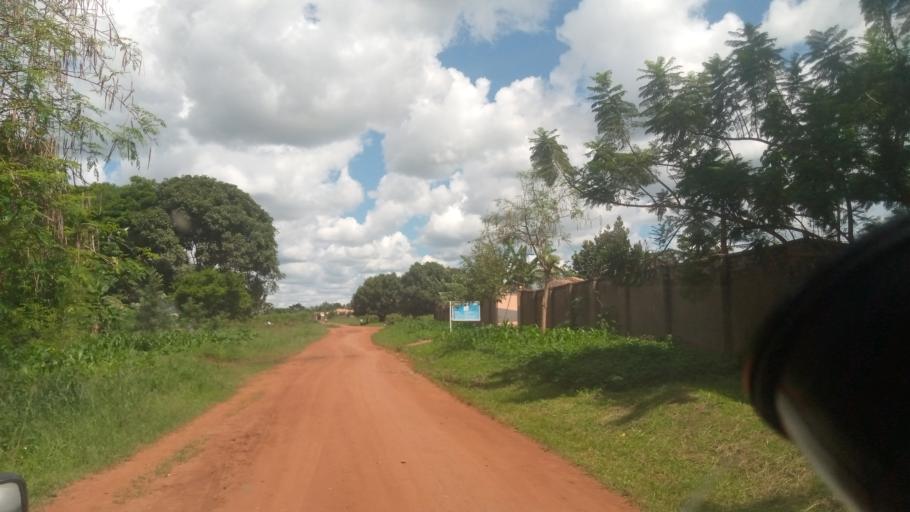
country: UG
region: Northern Region
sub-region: Lira District
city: Lira
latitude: 2.2366
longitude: 32.9069
